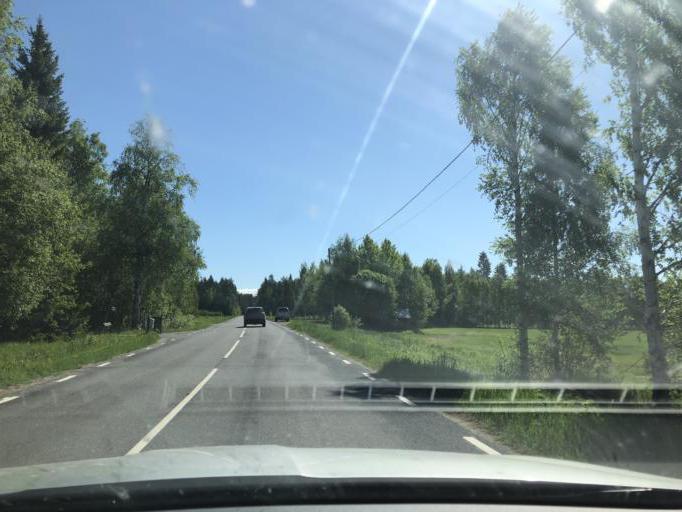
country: SE
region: Norrbotten
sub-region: Lulea Kommun
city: Gammelstad
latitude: 65.6568
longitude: 22.0004
